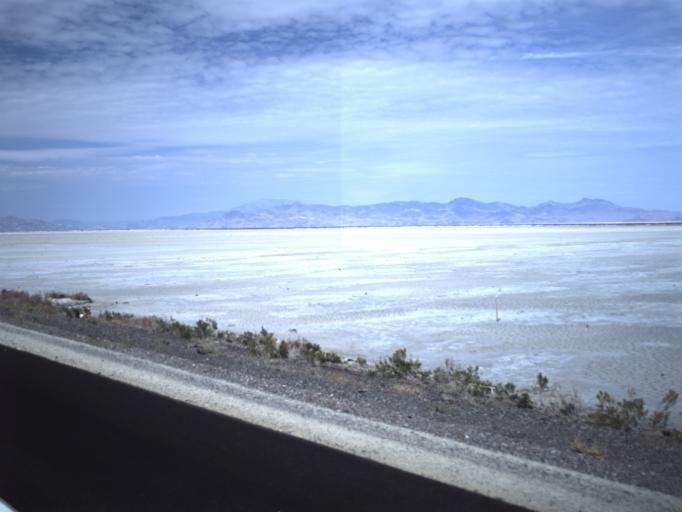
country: US
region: Utah
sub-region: Tooele County
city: Wendover
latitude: 40.7322
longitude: -113.5145
